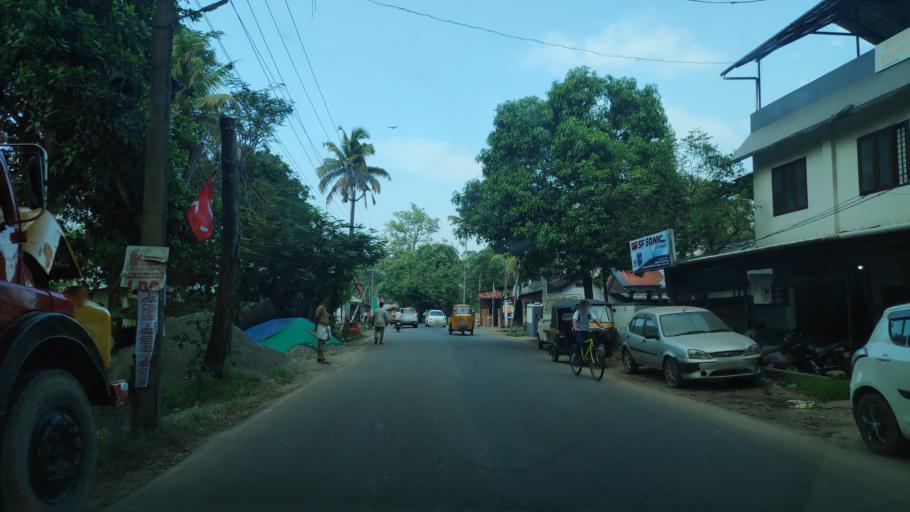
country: IN
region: Kerala
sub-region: Alappuzha
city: Alleppey
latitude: 9.5673
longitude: 76.3478
